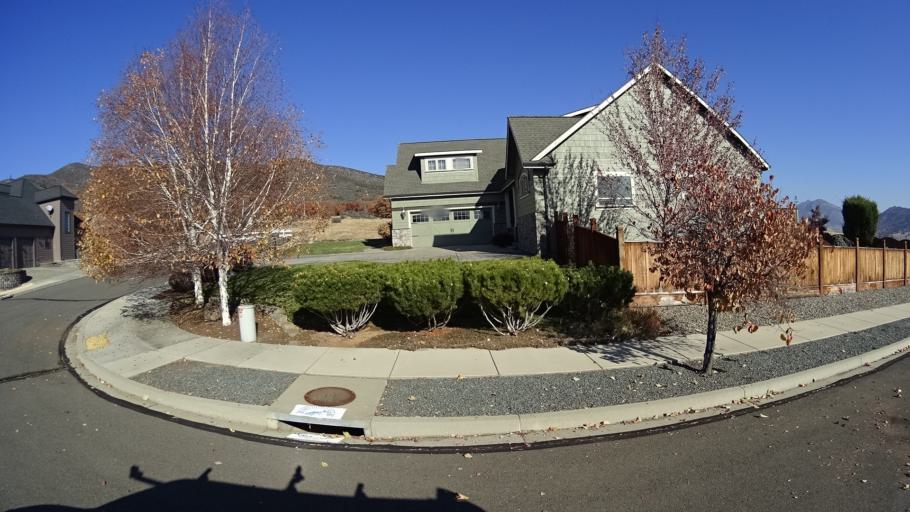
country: US
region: California
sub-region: Siskiyou County
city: Yreka
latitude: 41.7456
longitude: -122.6419
